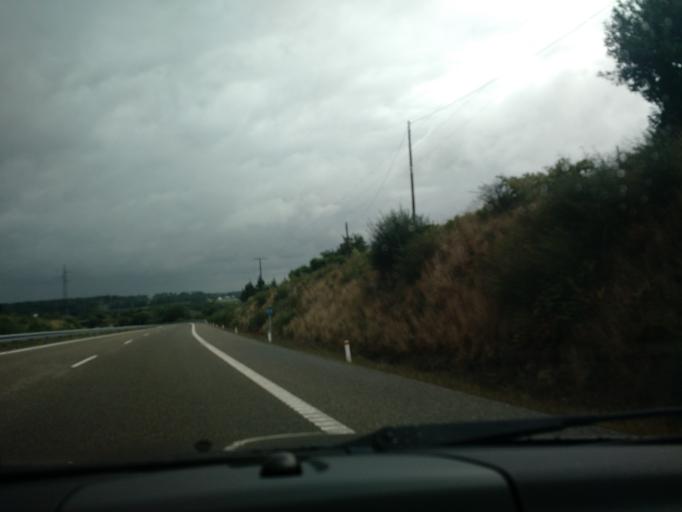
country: ES
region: Galicia
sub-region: Provincia da Coruna
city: Oroso
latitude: 42.9619
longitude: -8.4560
